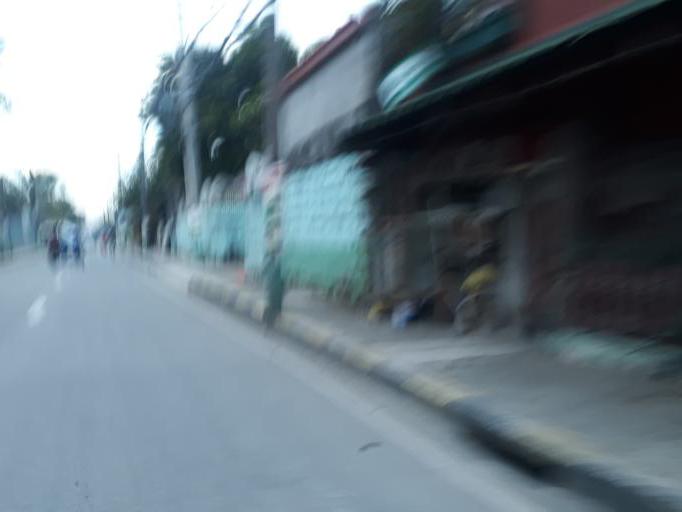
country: PH
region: Calabarzon
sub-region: Province of Rizal
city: Valenzuela
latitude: 14.7078
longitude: 120.9526
